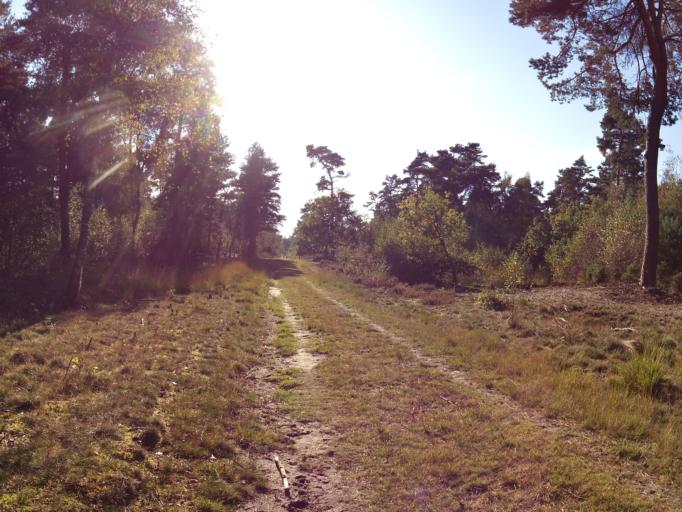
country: NL
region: Limburg
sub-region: Gemeente Bergen
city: Wellerlooi
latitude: 51.5260
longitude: 6.1586
